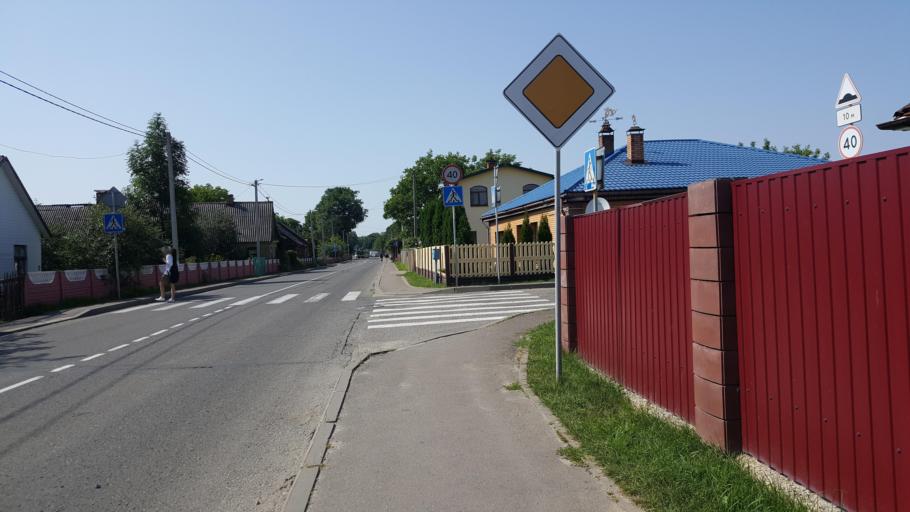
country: BY
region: Brest
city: Zhabinka
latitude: 52.1972
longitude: 24.0219
